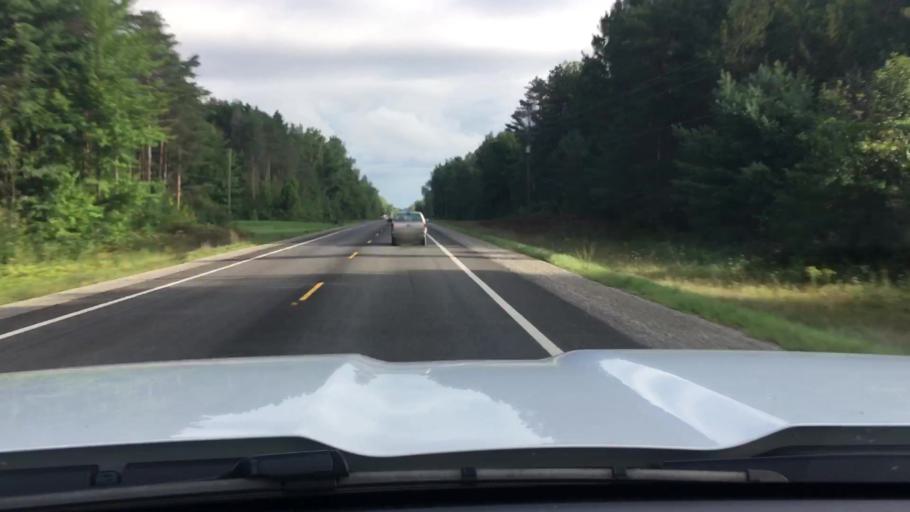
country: US
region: Michigan
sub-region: Tuscola County
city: Caro
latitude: 43.4280
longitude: -83.3847
